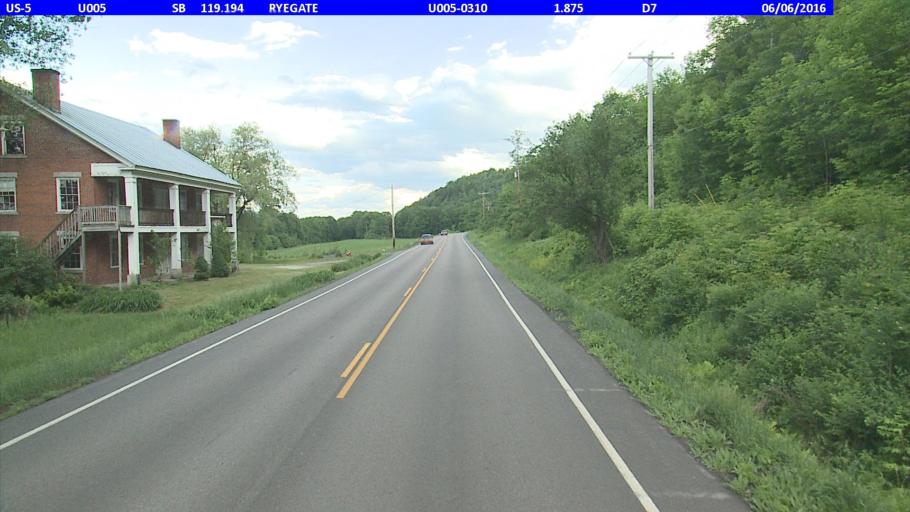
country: US
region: New Hampshire
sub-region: Grafton County
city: Woodsville
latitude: 44.1817
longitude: -72.0615
